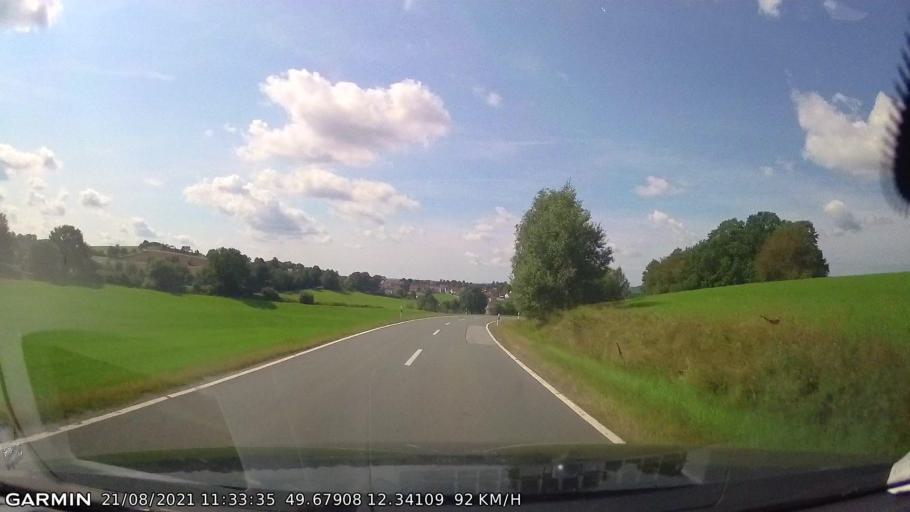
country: DE
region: Bavaria
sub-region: Upper Palatinate
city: Waldthurn
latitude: 49.6789
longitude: 12.3409
